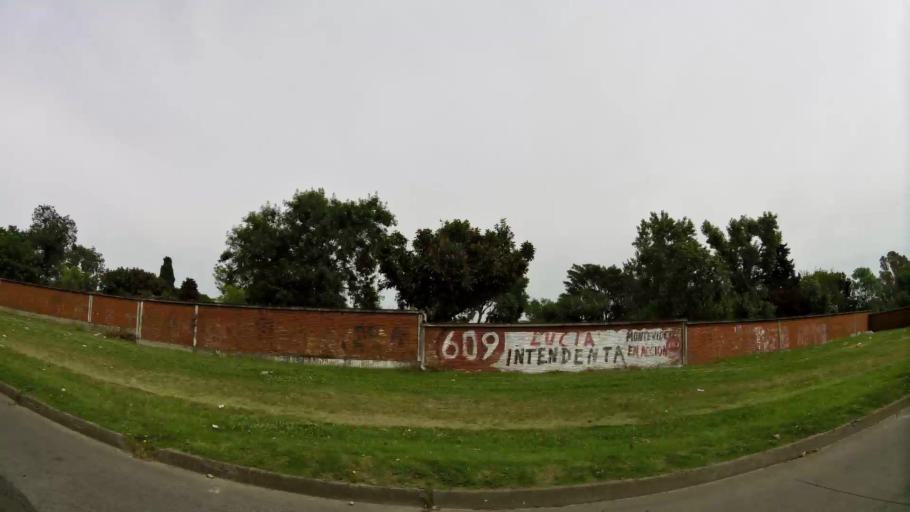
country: UY
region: Montevideo
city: Montevideo
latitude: -34.8437
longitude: -56.1734
